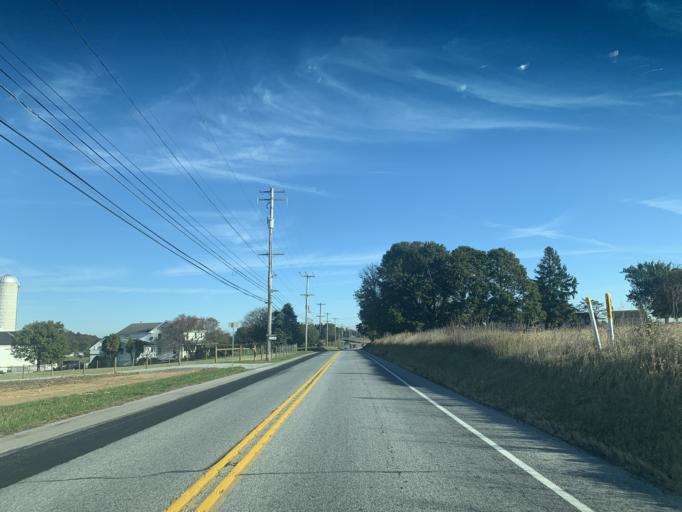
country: US
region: Pennsylvania
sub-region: Chester County
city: Oxford
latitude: 39.8500
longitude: -75.9348
